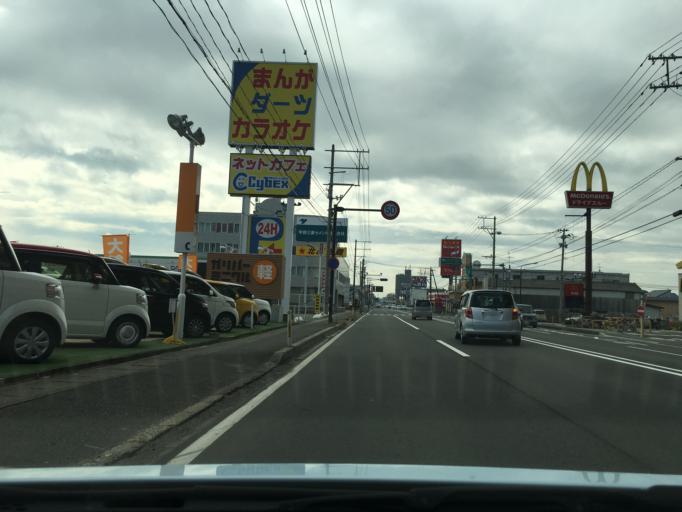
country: JP
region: Fukushima
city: Koriyama
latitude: 37.3663
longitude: 140.3700
